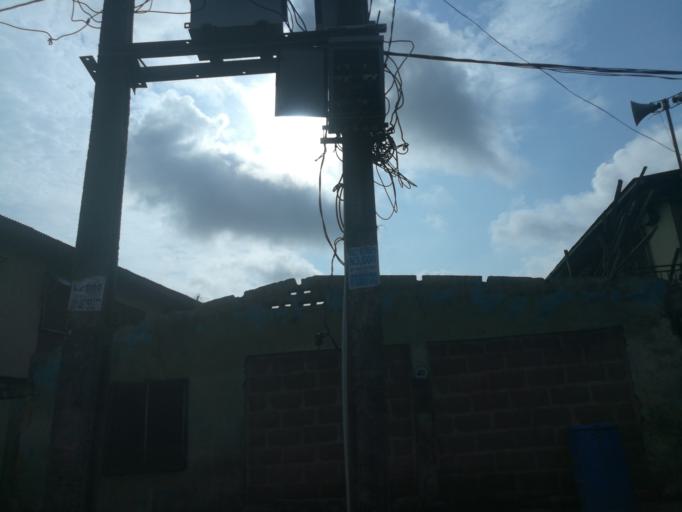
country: NG
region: Lagos
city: Agege
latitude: 6.6146
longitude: 3.3137
